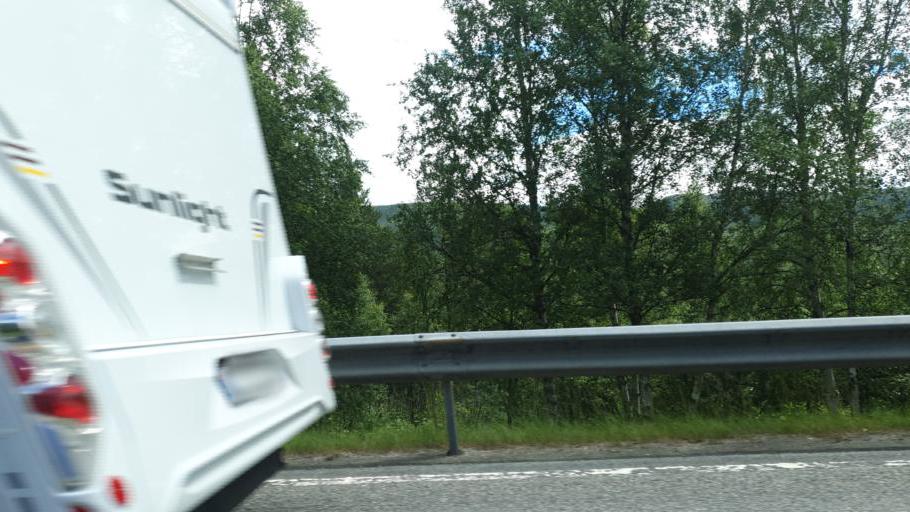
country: NO
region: Sor-Trondelag
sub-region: Rennebu
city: Berkak
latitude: 62.6714
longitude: 9.9095
